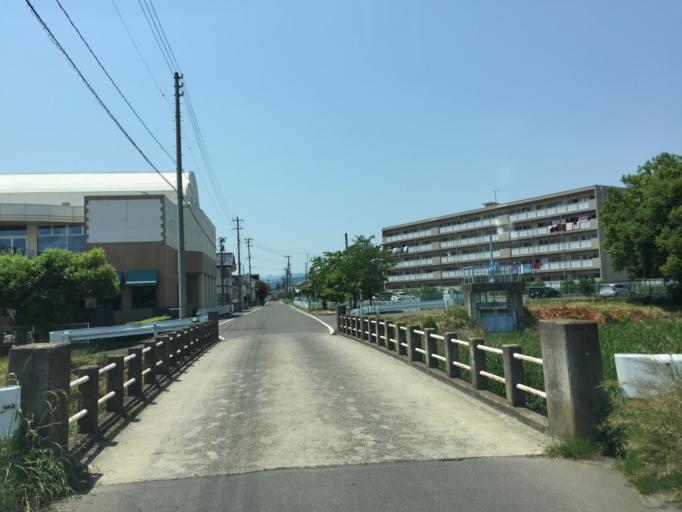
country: JP
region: Fukushima
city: Hobaramachi
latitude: 37.8261
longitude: 140.5545
